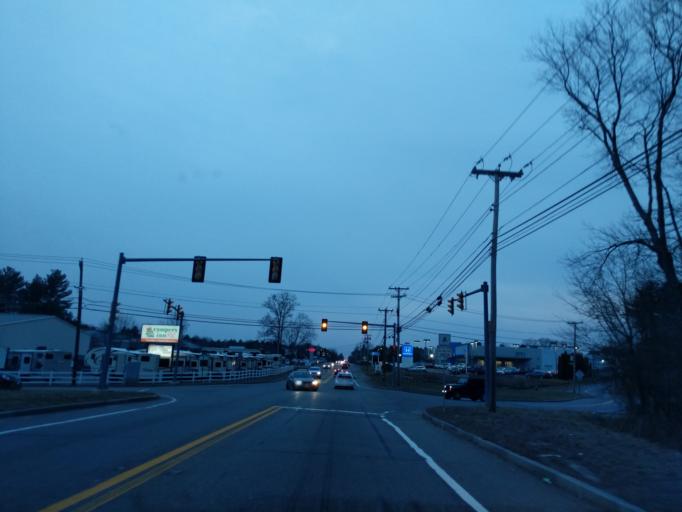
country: US
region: Massachusetts
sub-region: Bristol County
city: Raynham Center
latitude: 41.9037
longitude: -71.0058
